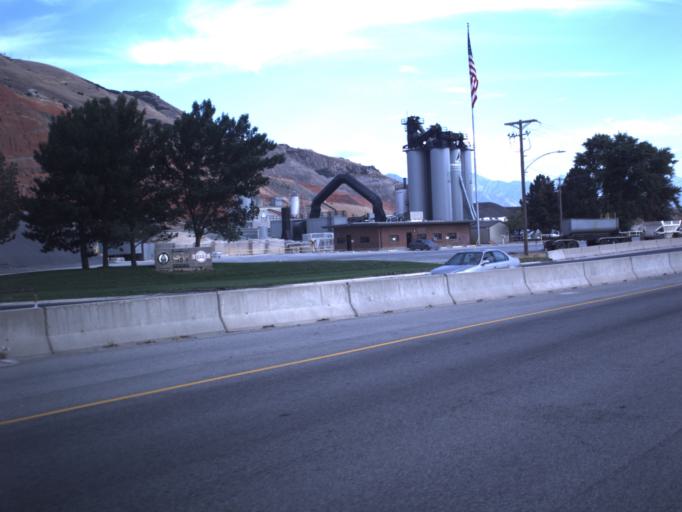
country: US
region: Utah
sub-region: Davis County
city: North Salt Lake
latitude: 40.8132
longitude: -111.9191
